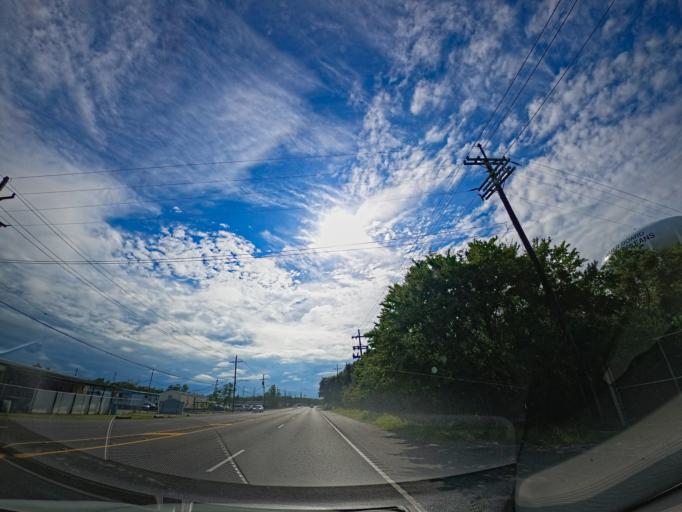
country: US
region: Louisiana
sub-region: Saint Bernard Parish
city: Chalmette
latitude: 30.0435
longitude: -89.8940
